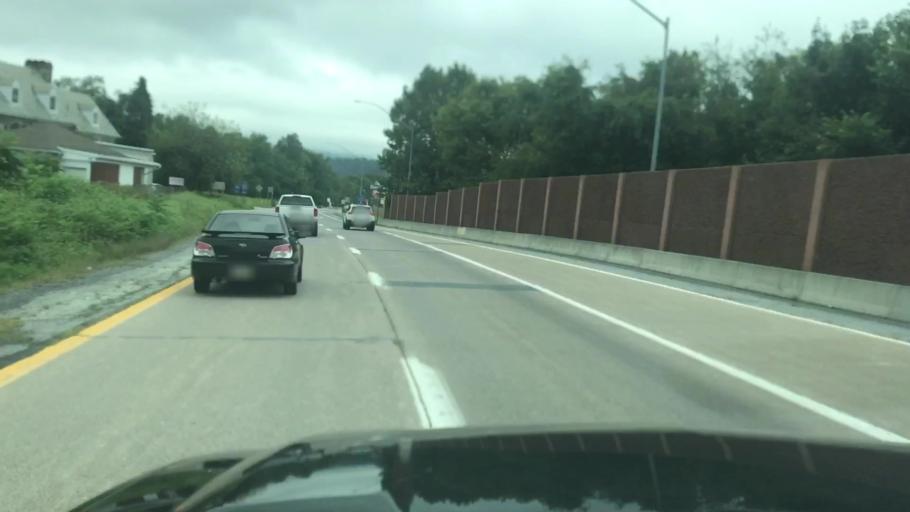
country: US
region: Pennsylvania
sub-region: Cumberland County
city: West Fairview
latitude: 40.3137
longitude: -76.8984
